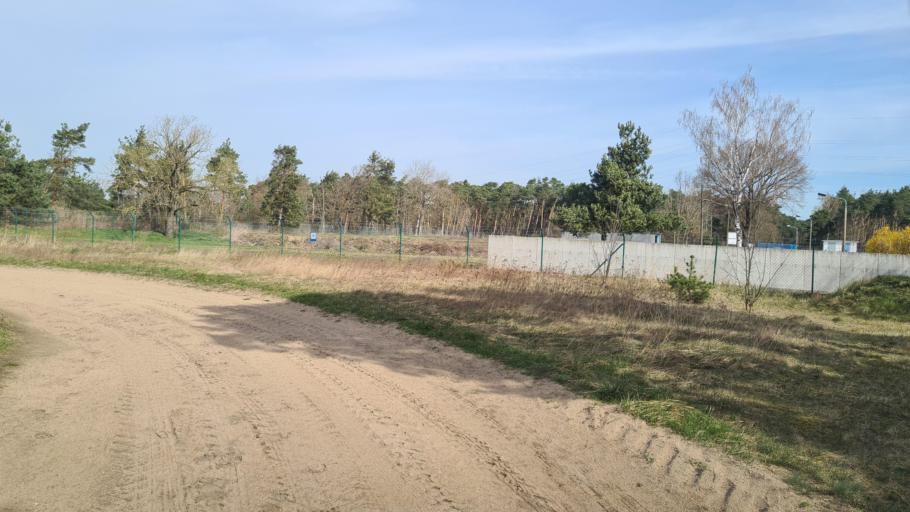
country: DE
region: Saxony
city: Nauwalde
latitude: 51.4655
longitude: 13.3985
